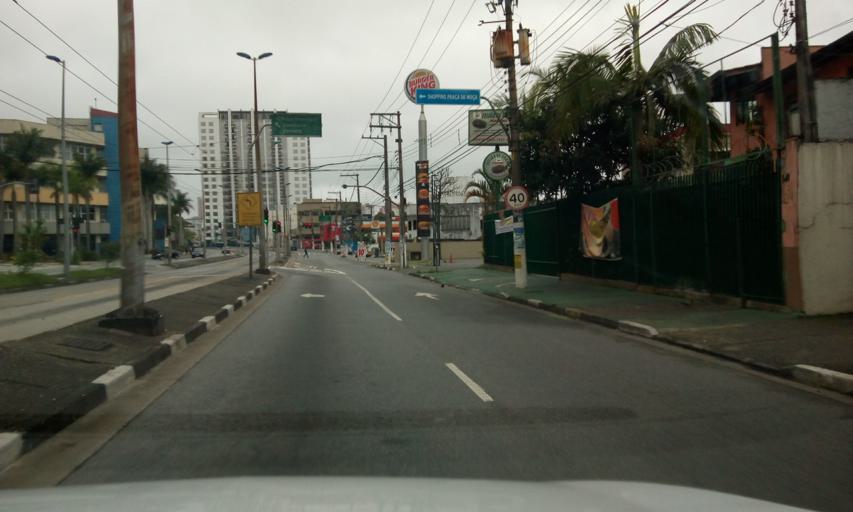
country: BR
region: Sao Paulo
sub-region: Diadema
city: Diadema
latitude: -23.6858
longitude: -46.6158
